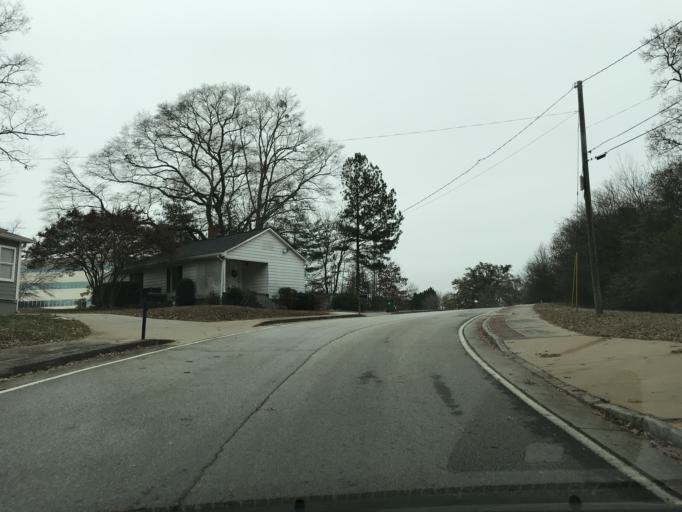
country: US
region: Georgia
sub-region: DeKalb County
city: Clarkston
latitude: 33.8273
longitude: -84.2471
